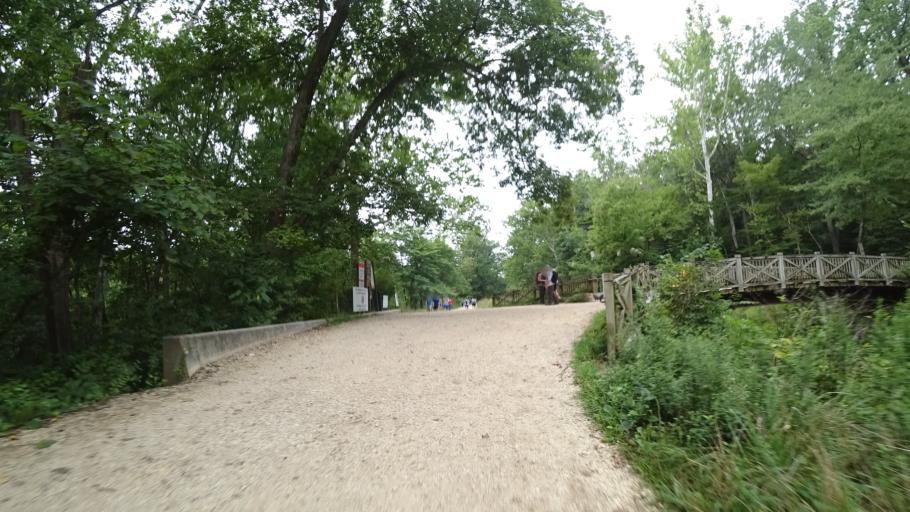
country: US
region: Maryland
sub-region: Montgomery County
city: Potomac
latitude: 38.9813
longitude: -77.2280
